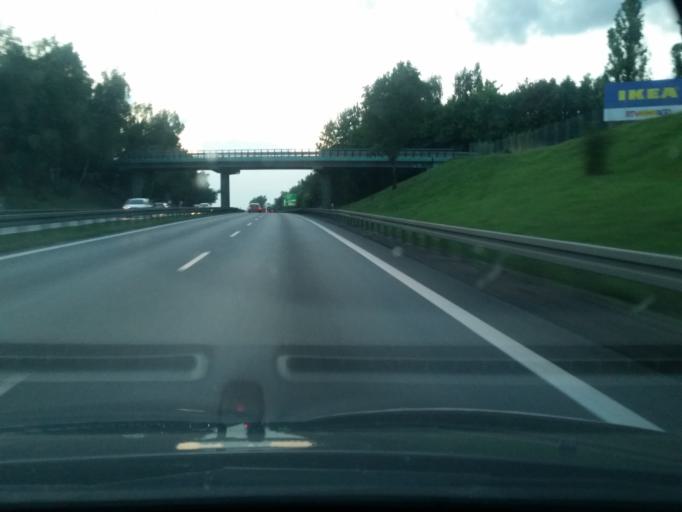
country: PL
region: Pomeranian Voivodeship
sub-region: Powiat gdanski
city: Kowale
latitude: 54.3348
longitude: 18.5328
